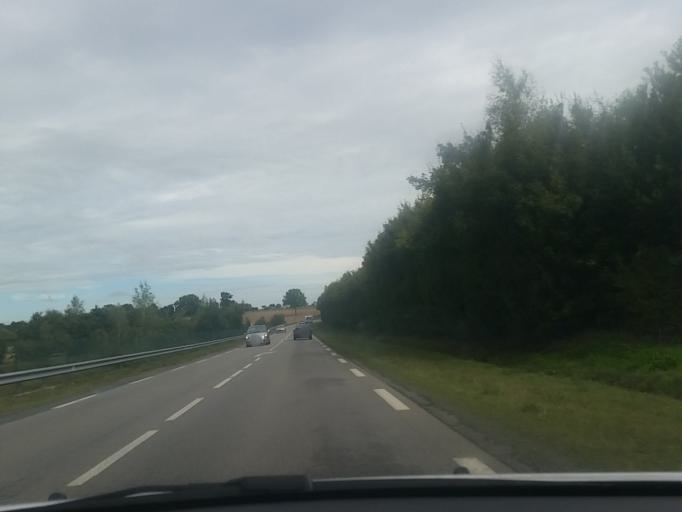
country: FR
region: Brittany
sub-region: Departement d'Ille-et-Vilaine
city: Martigne-Ferchaud
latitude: 47.8110
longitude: -1.3288
